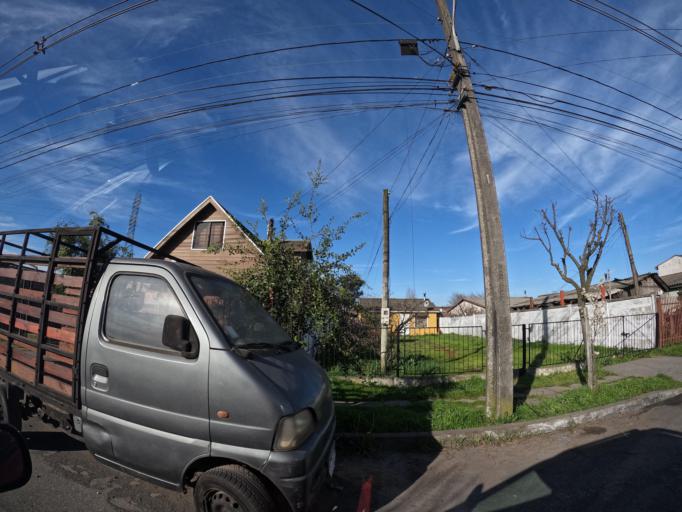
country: CL
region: Biobio
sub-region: Provincia de Concepcion
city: Talcahuano
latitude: -36.7705
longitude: -73.0822
